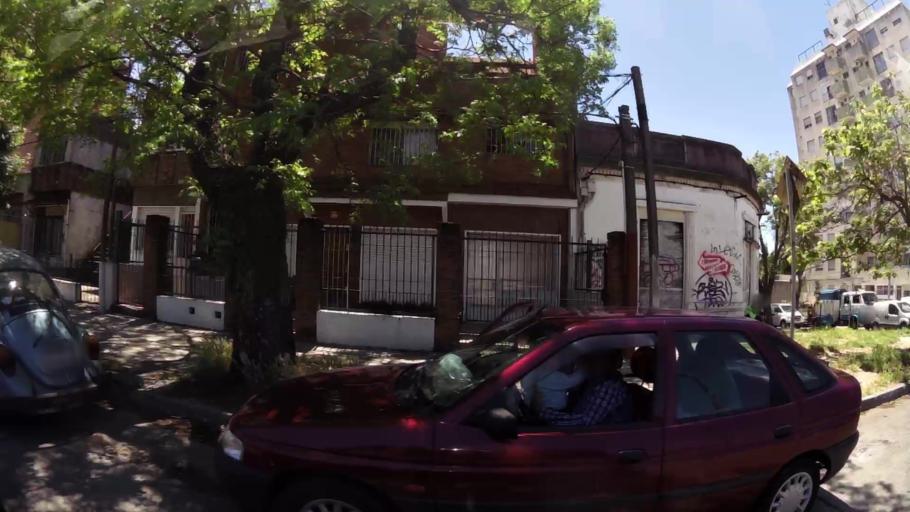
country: UY
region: Montevideo
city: Montevideo
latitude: -34.8966
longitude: -56.1255
